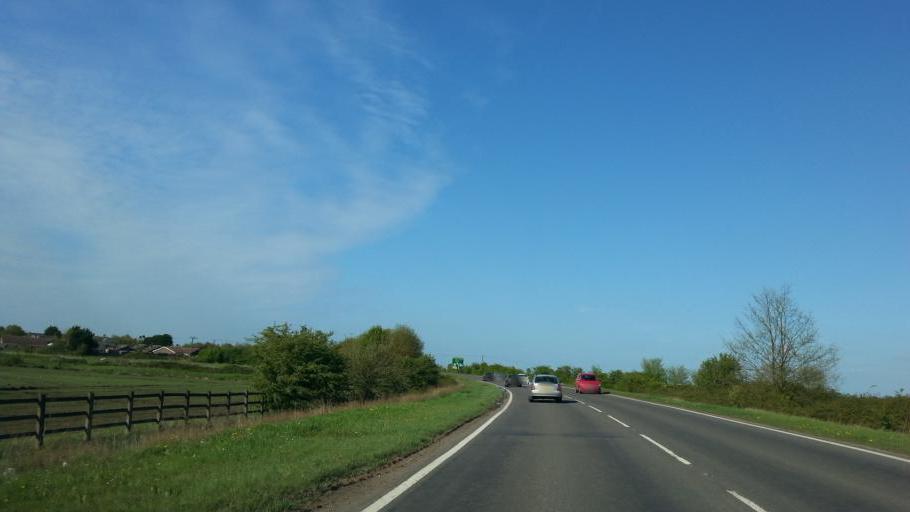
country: GB
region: England
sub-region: Cambridgeshire
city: Chatteris
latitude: 52.4524
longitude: 0.0639
